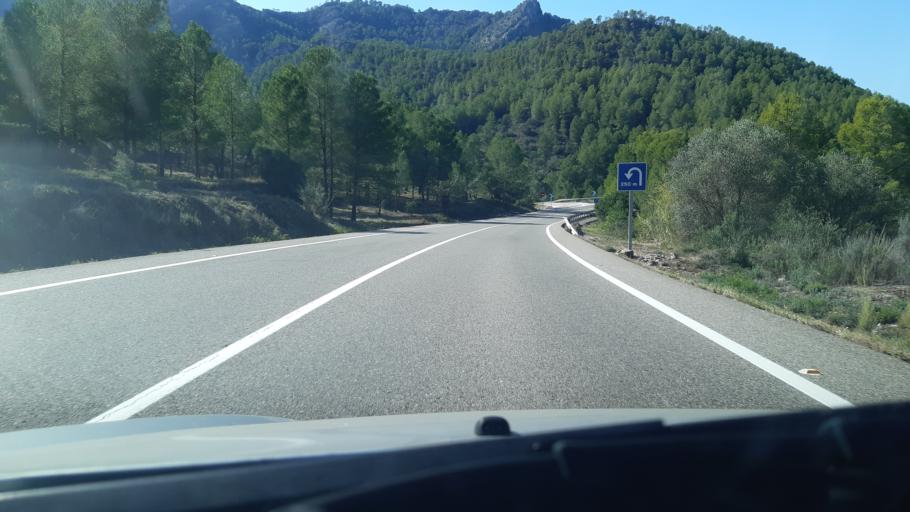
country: ES
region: Catalonia
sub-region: Provincia de Tarragona
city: Rasquera
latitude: 40.9937
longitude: 0.5618
